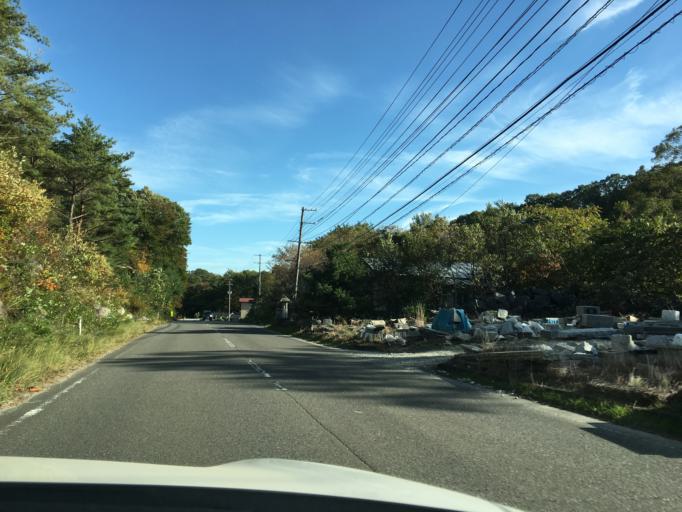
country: JP
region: Fukushima
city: Funehikimachi-funehiki
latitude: 37.3310
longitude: 140.5857
